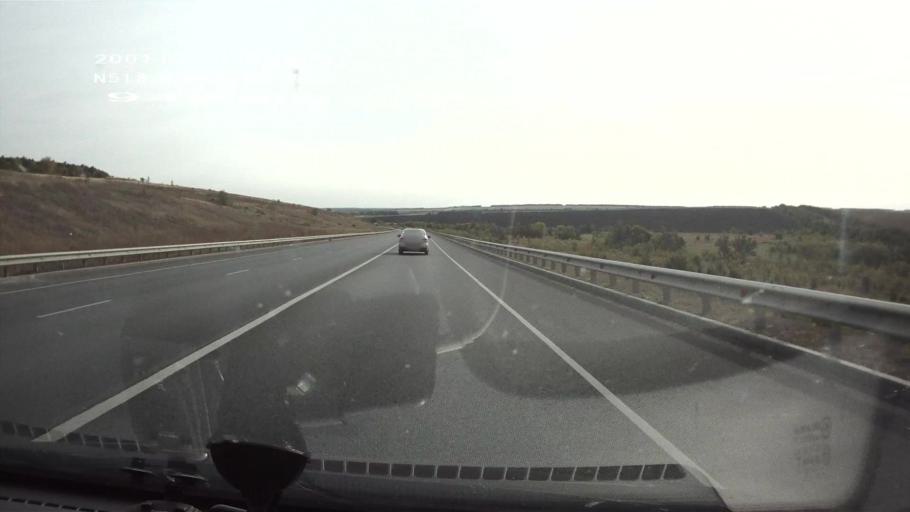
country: RU
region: Saratov
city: Yelshanka
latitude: 51.8778
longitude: 46.5078
